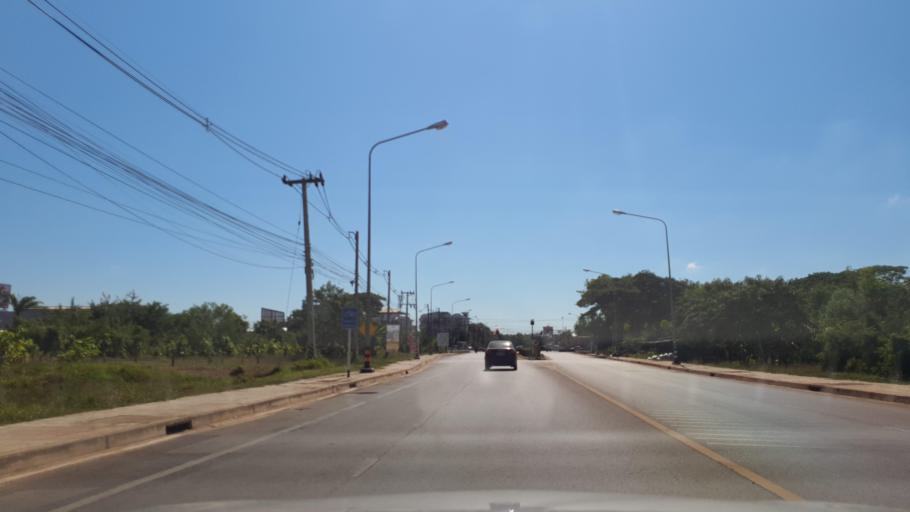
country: TH
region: Sakon Nakhon
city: Sakon Nakhon
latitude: 17.1499
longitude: 104.1292
